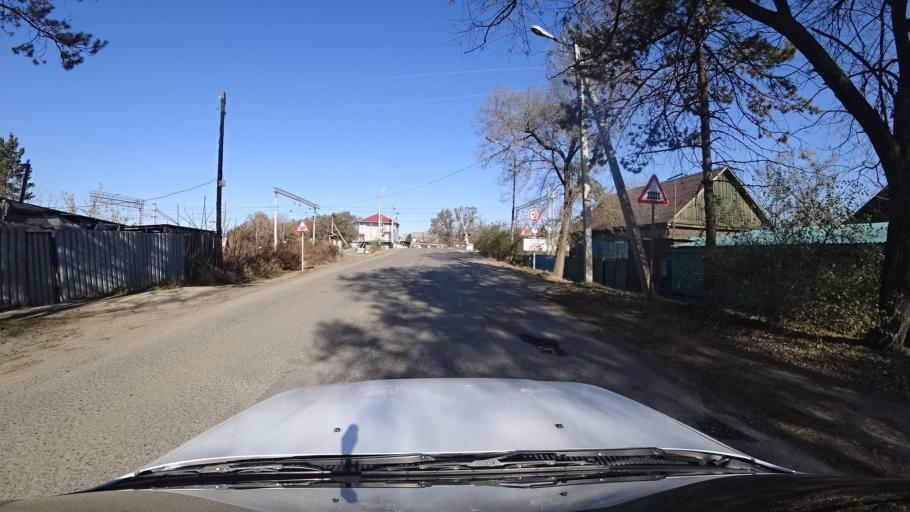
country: RU
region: Primorskiy
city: Dal'nerechensk
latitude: 45.9376
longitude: 133.7321
